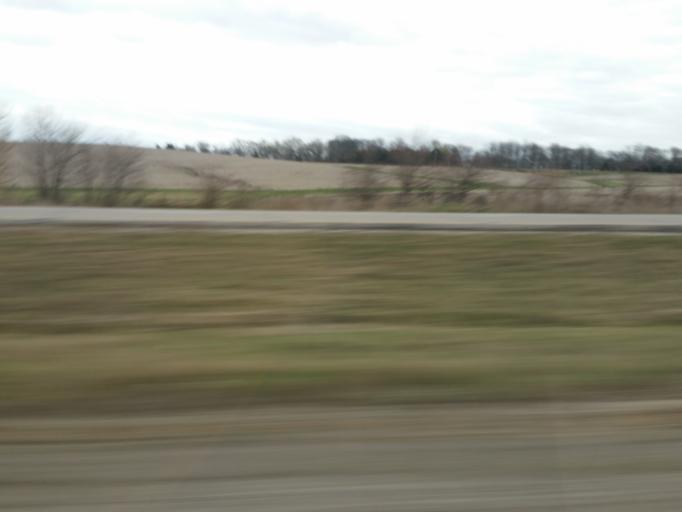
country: US
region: Iowa
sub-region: Johnson County
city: University Heights
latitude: 41.5947
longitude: -91.5469
